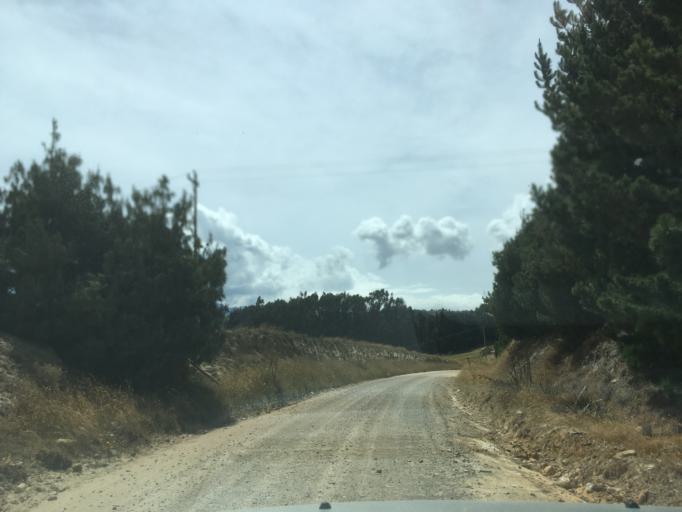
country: CO
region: Boyaca
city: Aquitania
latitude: 5.5637
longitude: -72.9505
